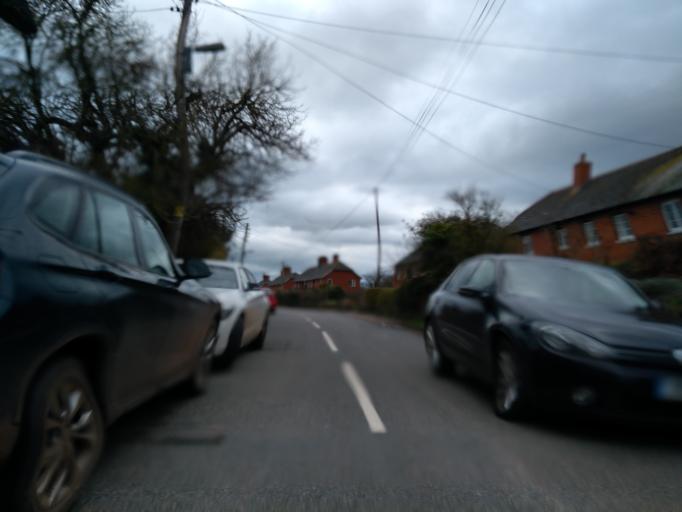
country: GB
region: England
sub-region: Devon
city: Exeter
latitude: 50.8077
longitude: -3.5238
